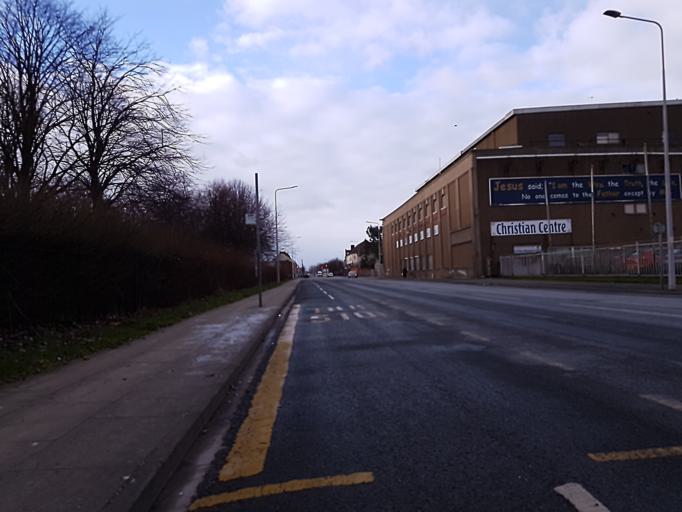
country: GB
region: England
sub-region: North East Lincolnshire
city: Grimsby
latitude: 53.5729
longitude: -0.0659
